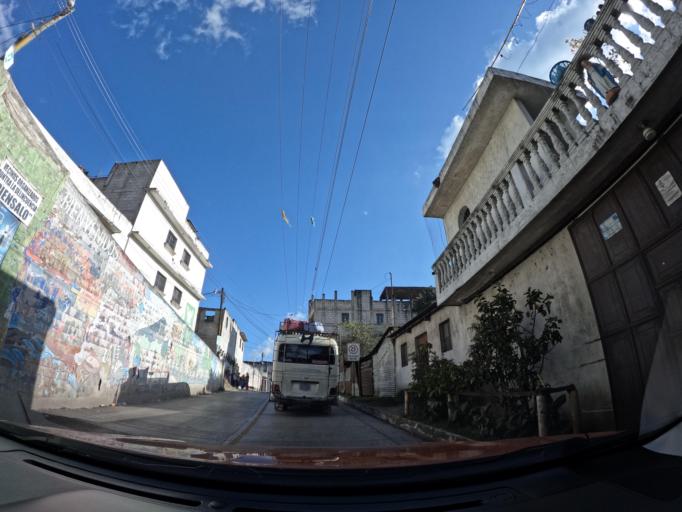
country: GT
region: Sacatepequez
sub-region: Municipio de Santa Maria de Jesus
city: Santa Maria de Jesus
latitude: 14.4983
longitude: -90.7106
